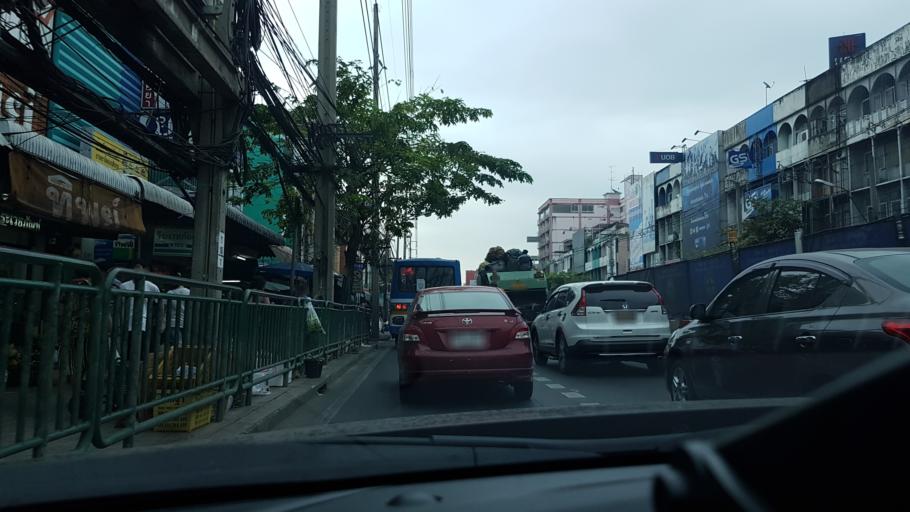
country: TH
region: Bangkok
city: Lat Phrao
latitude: 13.7966
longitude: 100.5909
